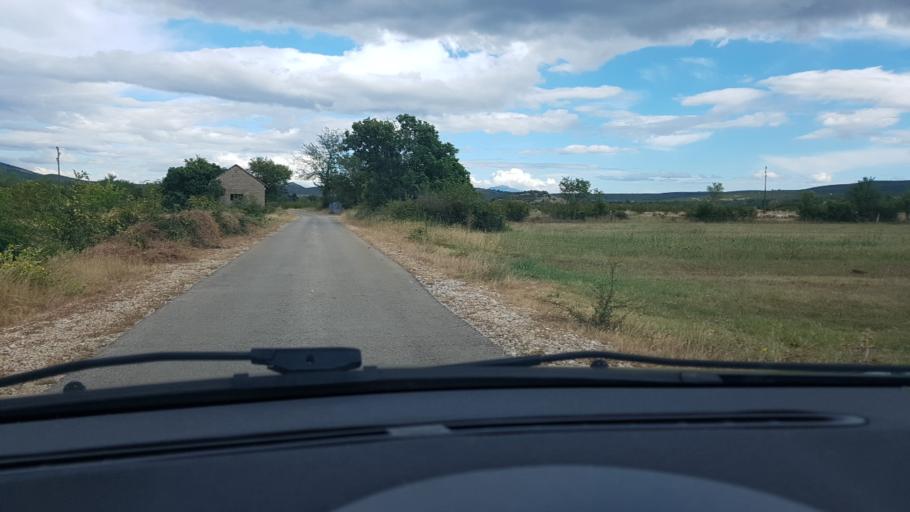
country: HR
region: Sibensko-Kniniska
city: Kistanje
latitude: 44.1085
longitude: 15.9299
